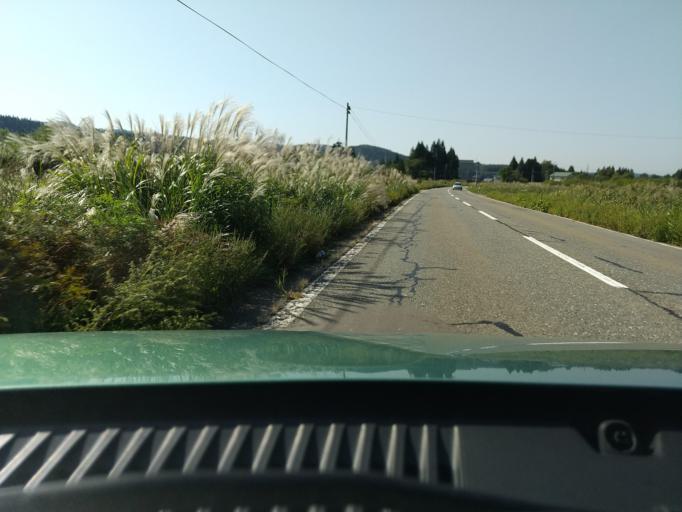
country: JP
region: Akita
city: Omagari
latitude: 39.6135
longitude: 140.3456
